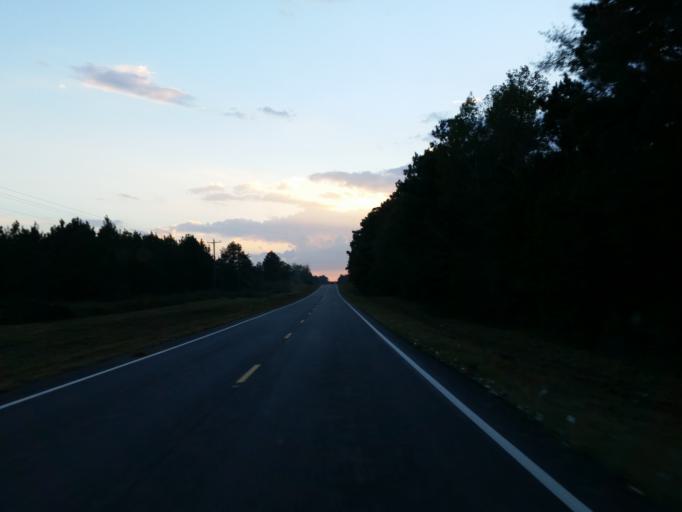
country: US
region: Georgia
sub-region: Pulaski County
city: Hawkinsville
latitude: 32.2310
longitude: -83.5122
